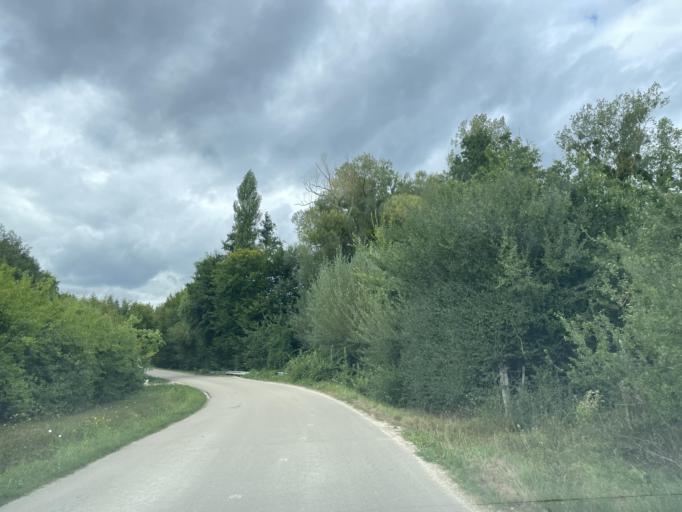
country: FR
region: Bourgogne
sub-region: Departement de l'Yonne
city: Charbuy
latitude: 47.8158
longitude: 3.4792
